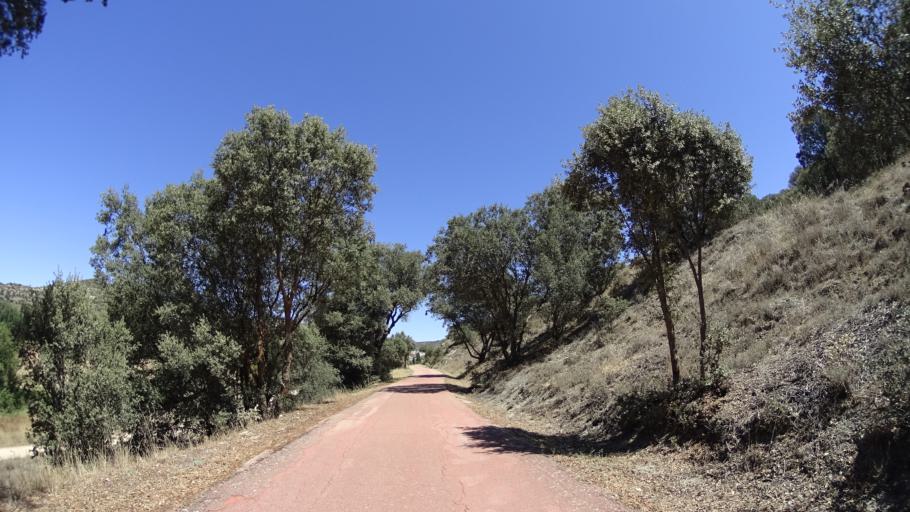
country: ES
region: Madrid
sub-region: Provincia de Madrid
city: Ambite
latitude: 40.3153
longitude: -3.1888
